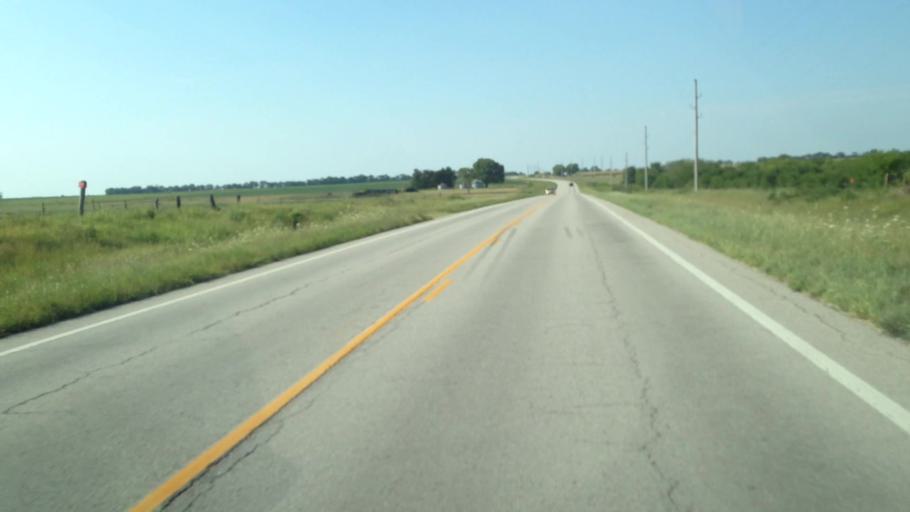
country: US
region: Kansas
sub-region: Allen County
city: Iola
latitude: 38.0010
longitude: -95.1704
